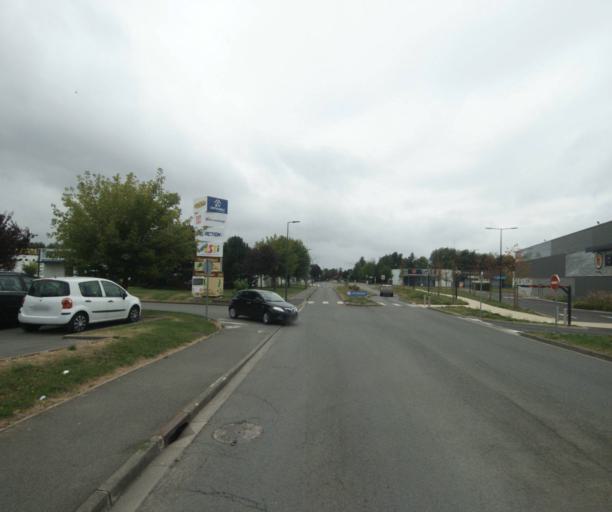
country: FR
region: Nord-Pas-de-Calais
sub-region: Departement du Nord
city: Lys-lez-Lannoy
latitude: 50.6783
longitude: 3.2230
